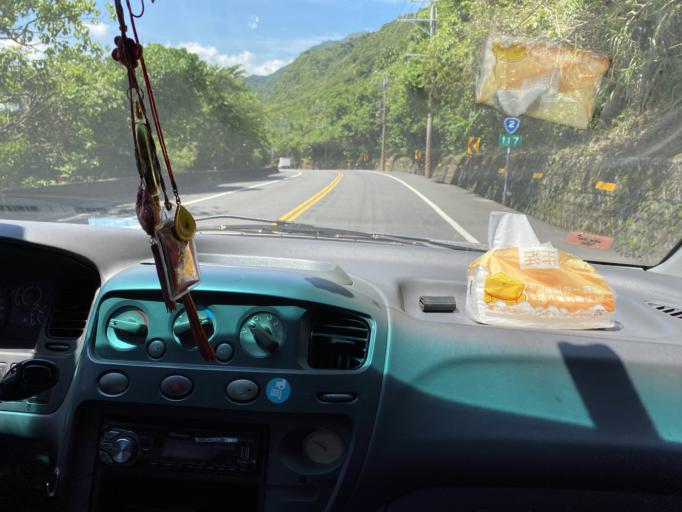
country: TW
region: Taiwan
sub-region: Keelung
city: Keelung
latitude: 24.9752
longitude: 121.9373
